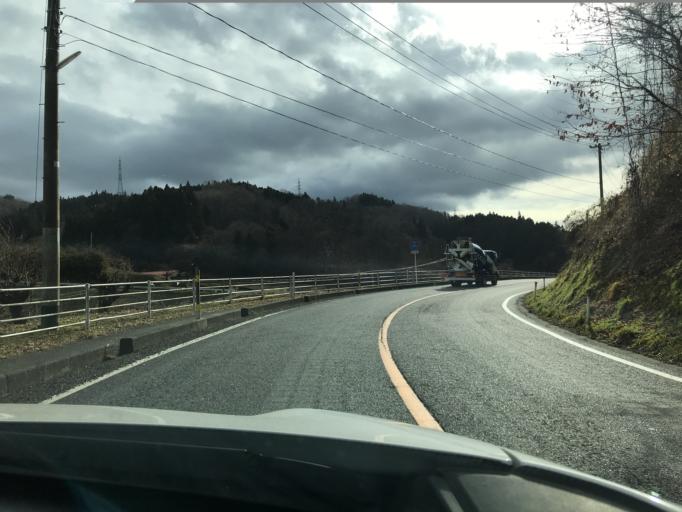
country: JP
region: Fukushima
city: Funehikimachi-funehiki
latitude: 37.5767
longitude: 140.5792
